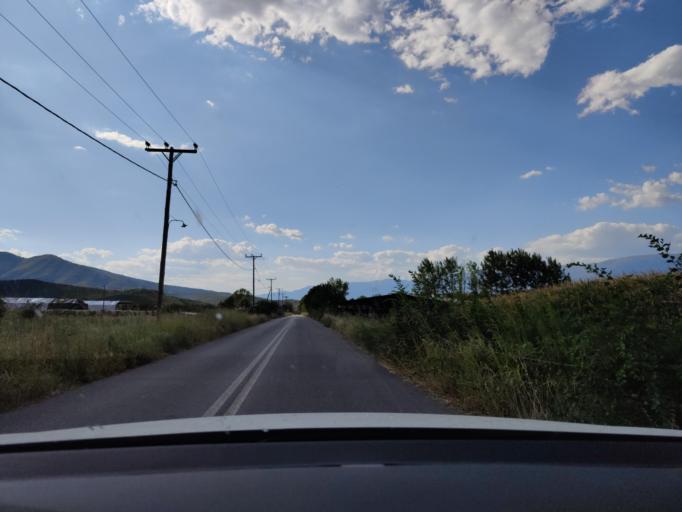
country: GR
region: Central Macedonia
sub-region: Nomos Serron
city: Chrysochorafa
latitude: 41.1798
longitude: 23.1099
